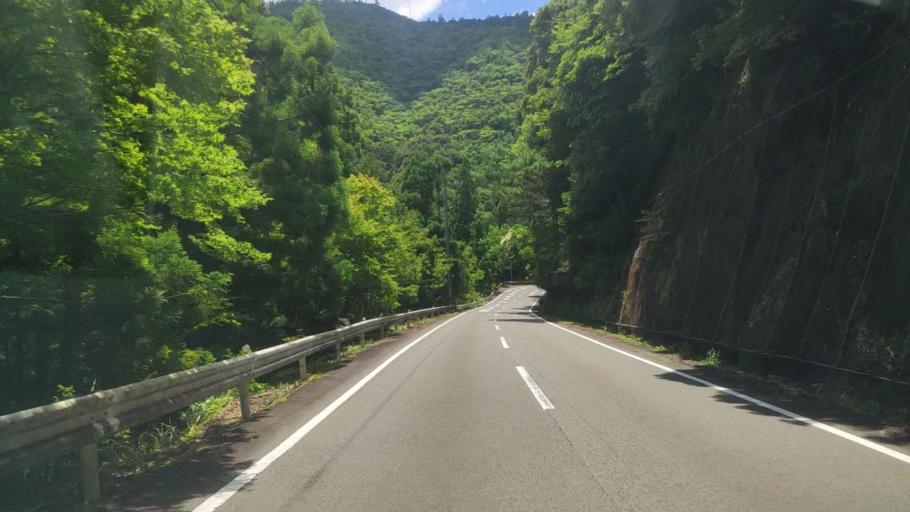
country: JP
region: Mie
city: Owase
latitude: 33.9961
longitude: 136.0142
